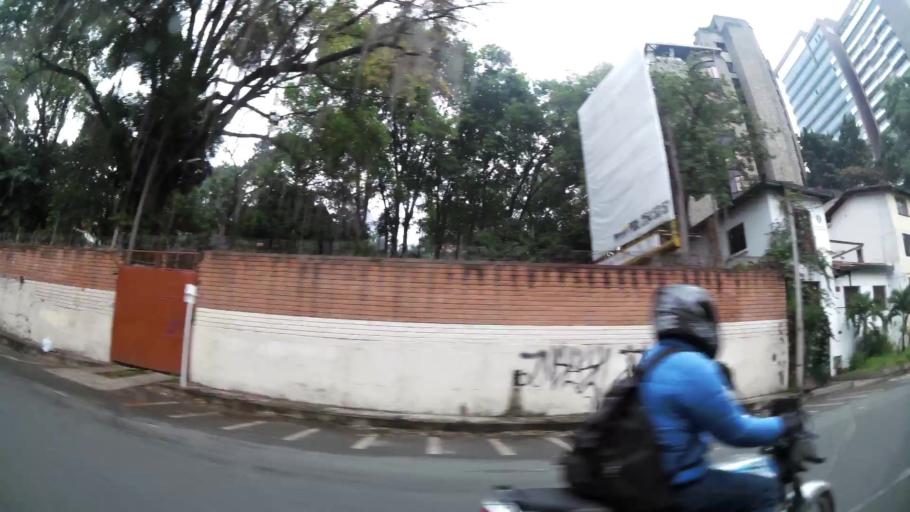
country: CO
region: Antioquia
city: Itagui
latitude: 6.2144
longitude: -75.5750
